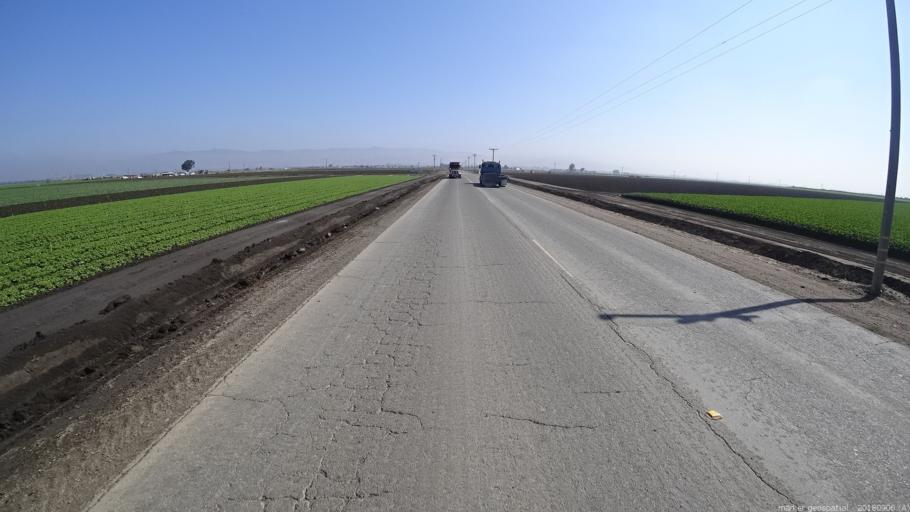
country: US
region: California
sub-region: Monterey County
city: Chualar
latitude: 36.5577
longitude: -121.5311
